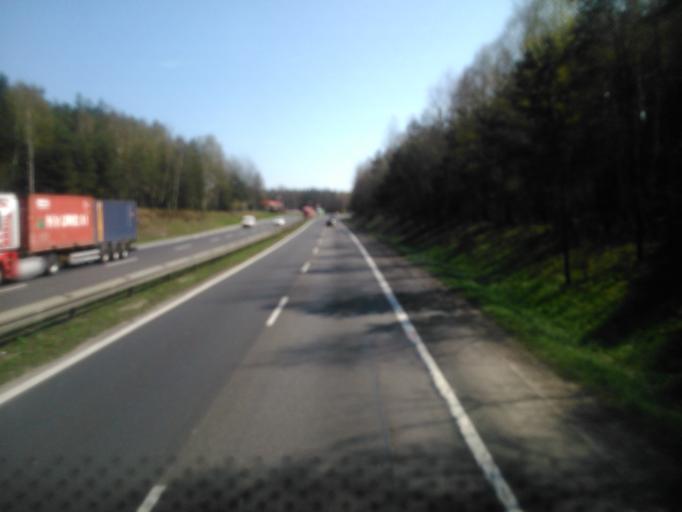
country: PL
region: Silesian Voivodeship
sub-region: Powiat czestochowski
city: Kamienica Polska
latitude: 50.6636
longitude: 19.1258
